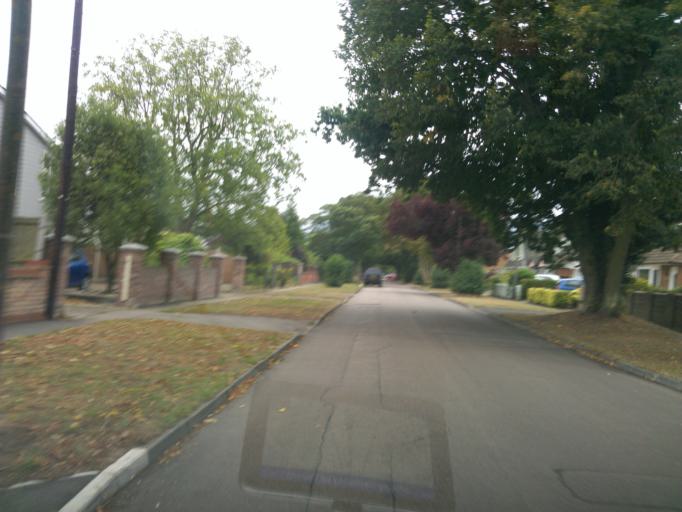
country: GB
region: England
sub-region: Essex
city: West Mersea
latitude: 51.7811
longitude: 0.9284
